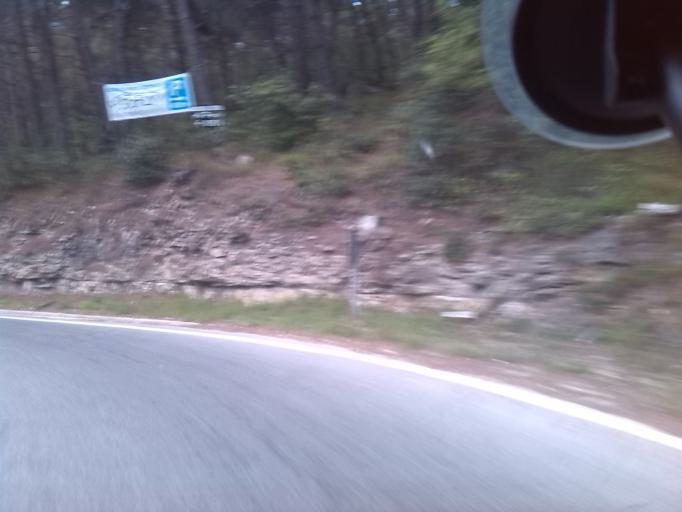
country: HR
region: Istarska
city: Novigrad
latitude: 45.3164
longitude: 13.6186
